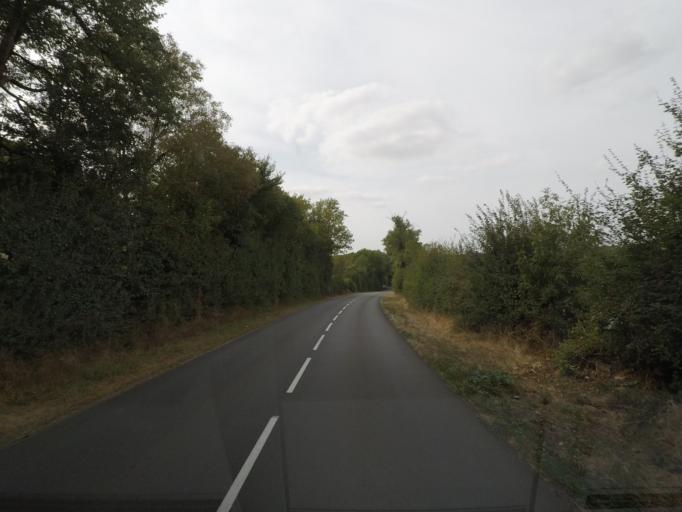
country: FR
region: Poitou-Charentes
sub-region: Departement de la Charente
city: Nanteuil-en-Vallee
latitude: 45.9965
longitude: 0.3307
